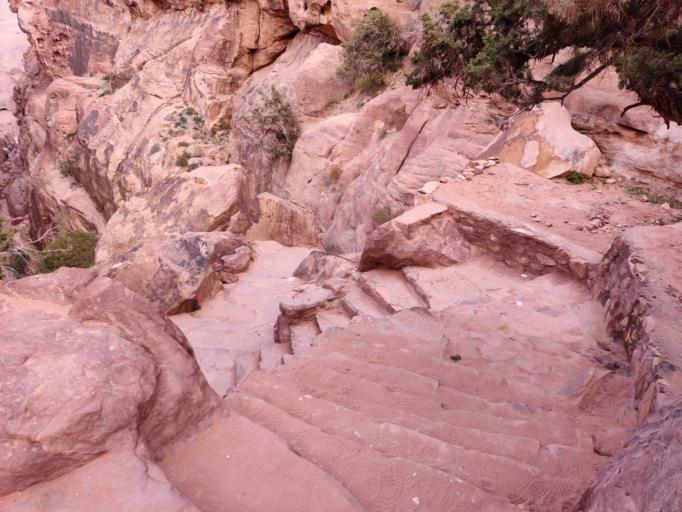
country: JO
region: Ma'an
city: Petra
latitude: 30.3205
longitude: 35.4486
